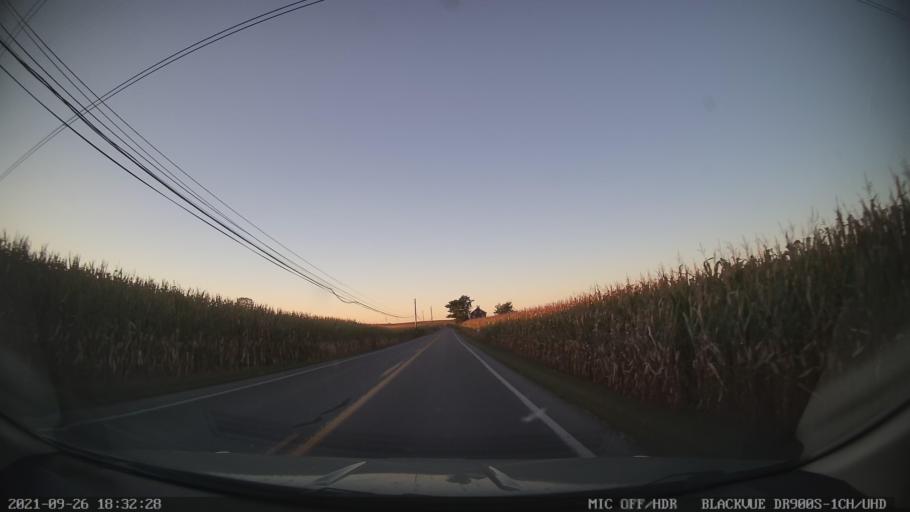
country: US
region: Pennsylvania
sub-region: Berks County
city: Kutztown
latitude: 40.4902
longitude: -75.7604
